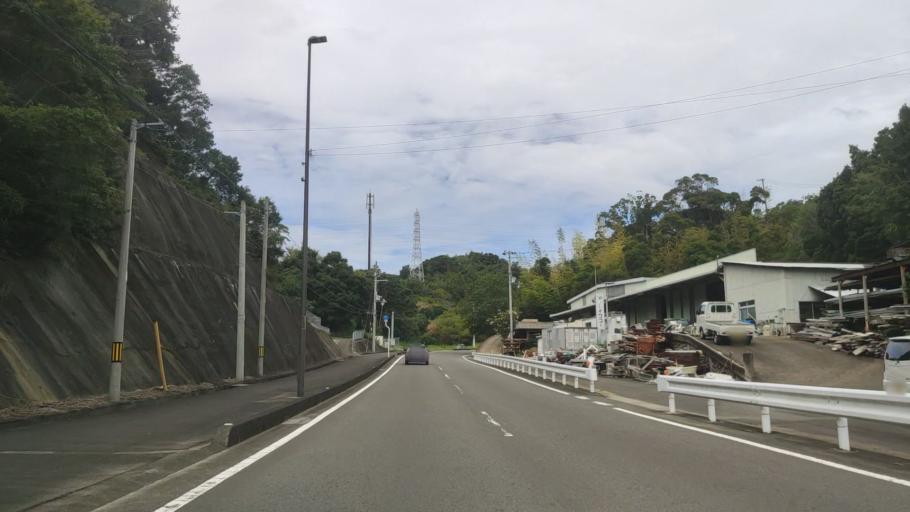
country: JP
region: Wakayama
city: Tanabe
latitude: 33.6835
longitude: 135.3881
